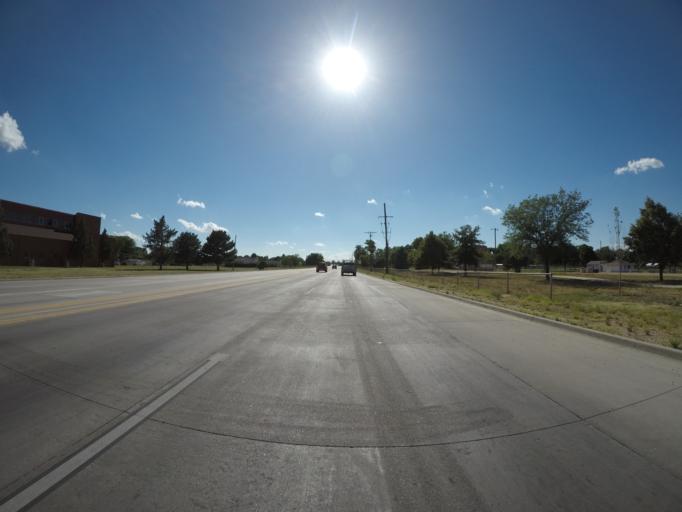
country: US
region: Colorado
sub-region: Logan County
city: Sterling
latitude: 40.6250
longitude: -103.2403
